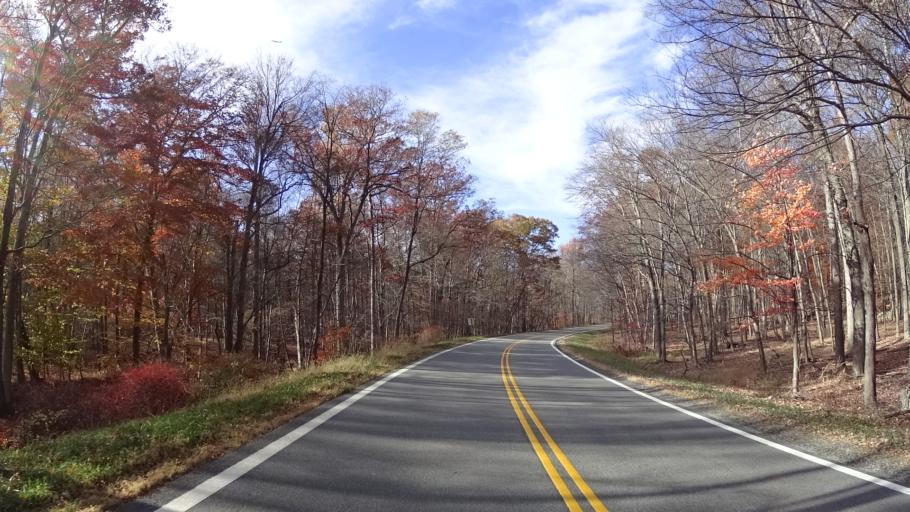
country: US
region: New Jersey
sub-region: Somerset County
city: Bernardsville
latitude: 40.7594
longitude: -74.5445
